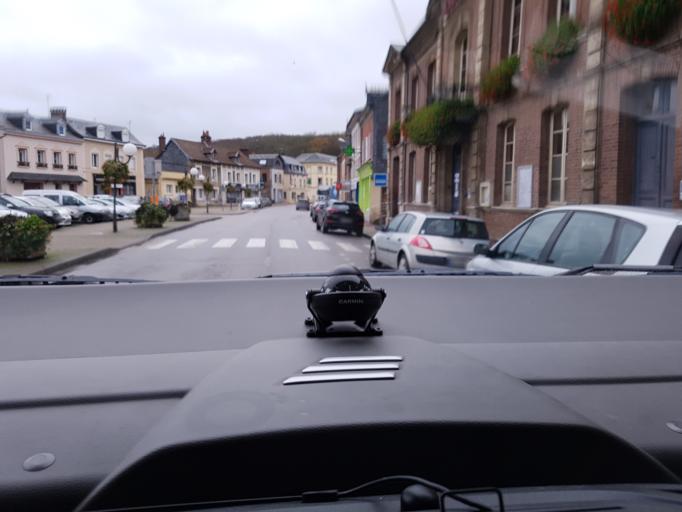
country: FR
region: Haute-Normandie
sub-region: Departement de l'Eure
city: Pont-Saint-Pierre
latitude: 49.3328
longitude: 1.2782
